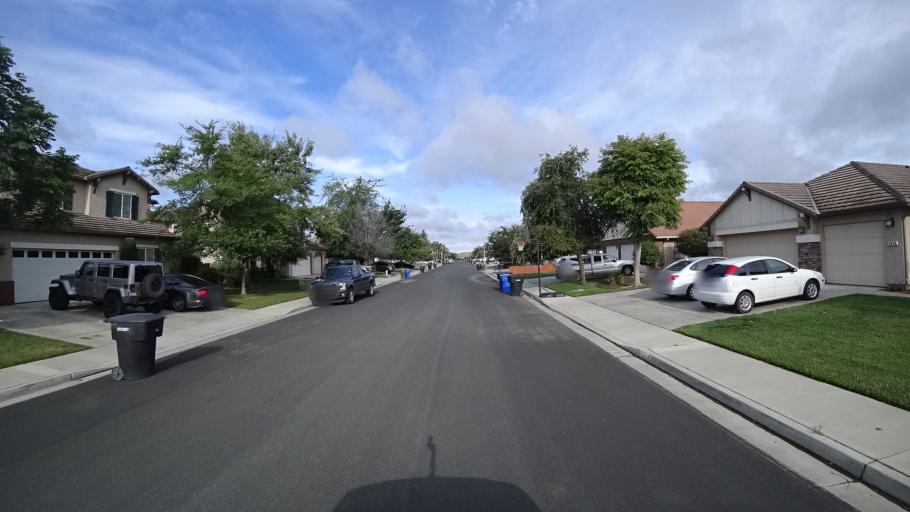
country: US
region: California
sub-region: Kings County
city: Lucerne
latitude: 36.3477
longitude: -119.6749
